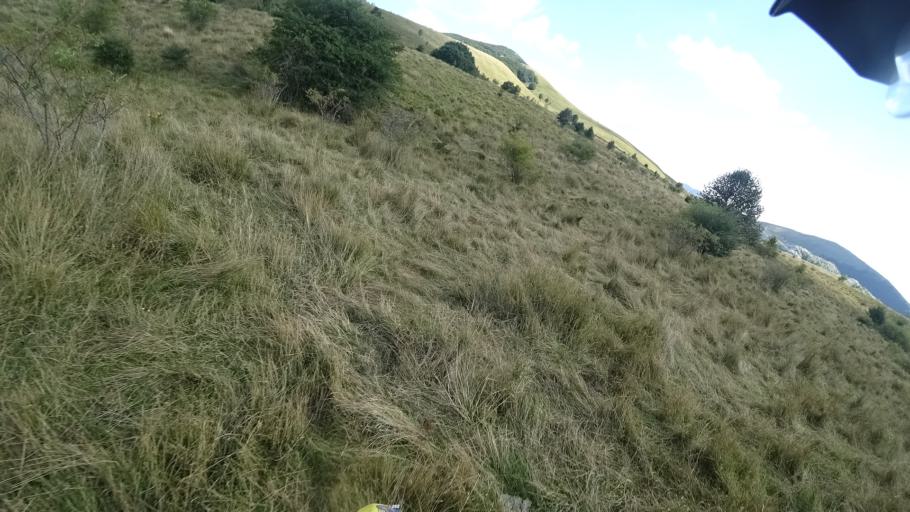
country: HR
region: Zadarska
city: Gracac
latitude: 44.4166
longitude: 16.0012
